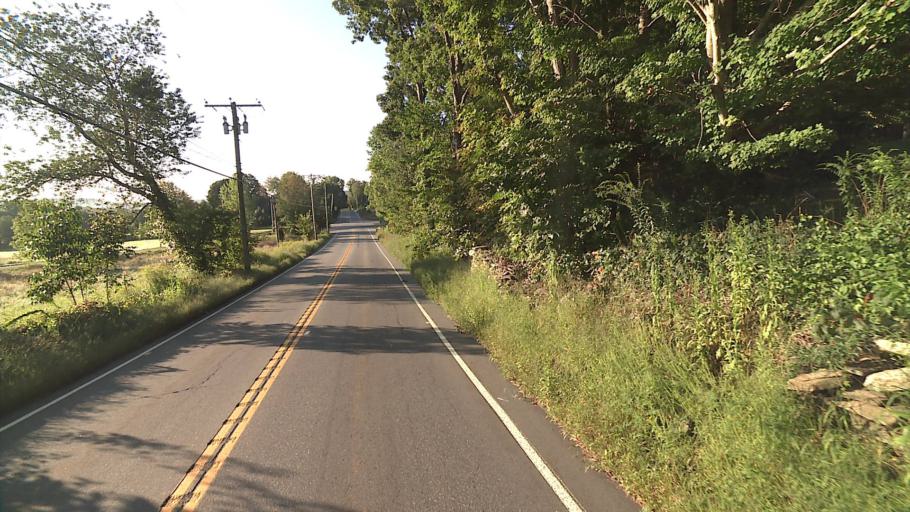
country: US
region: Connecticut
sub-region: Tolland County
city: South Coventry
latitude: 41.8051
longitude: -72.3037
